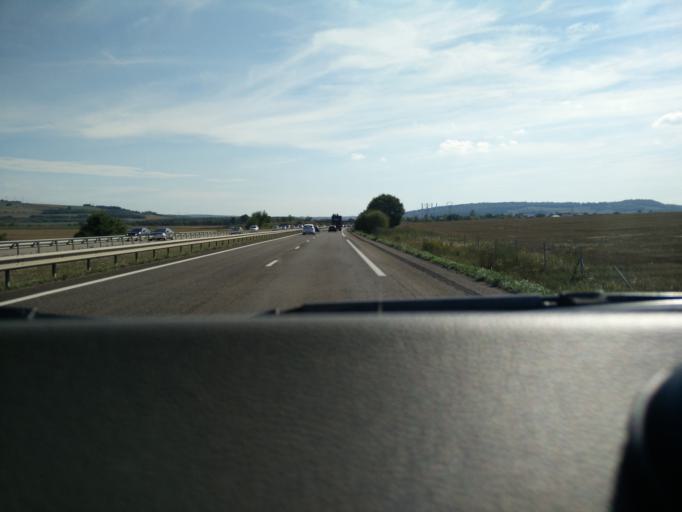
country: FR
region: Lorraine
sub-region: Departement de Meurthe-et-Moselle
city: Pont-a-Mousson
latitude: 48.8988
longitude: 6.1047
